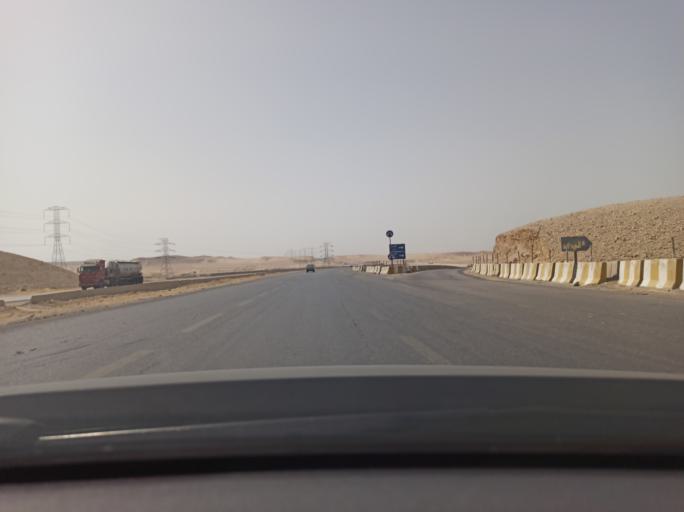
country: EG
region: Al Jizah
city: As Saff
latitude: 29.5318
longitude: 31.3869
